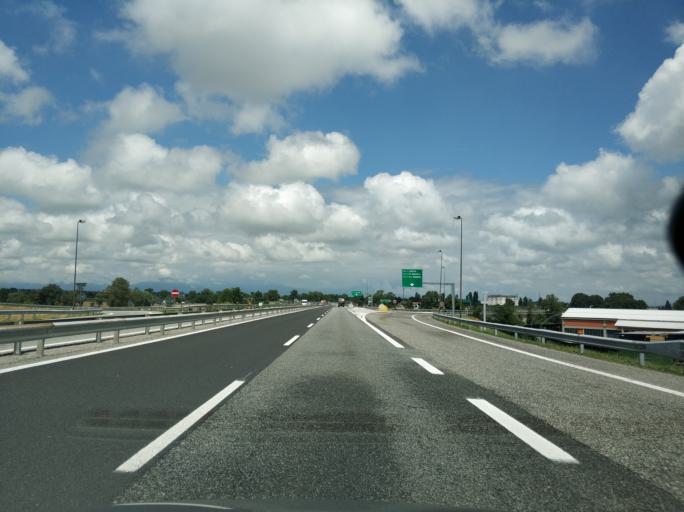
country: IT
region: Piedmont
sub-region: Provincia di Torino
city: Settimo Torinese
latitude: 45.1284
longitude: 7.7307
